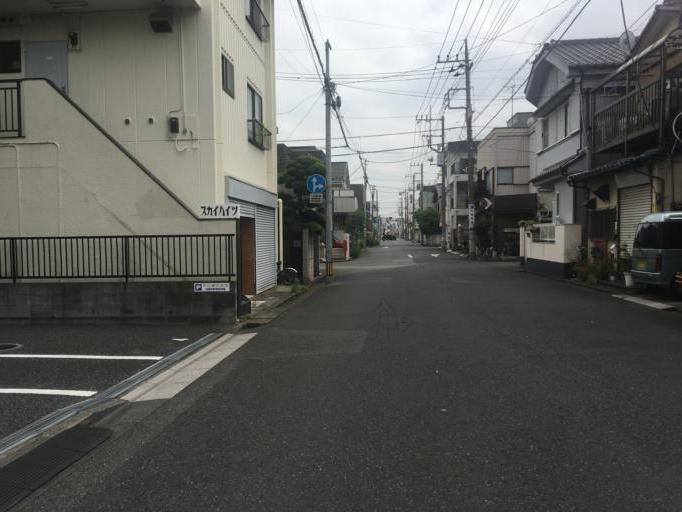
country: JP
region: Saitama
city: Shimotoda
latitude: 35.8307
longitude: 139.6974
